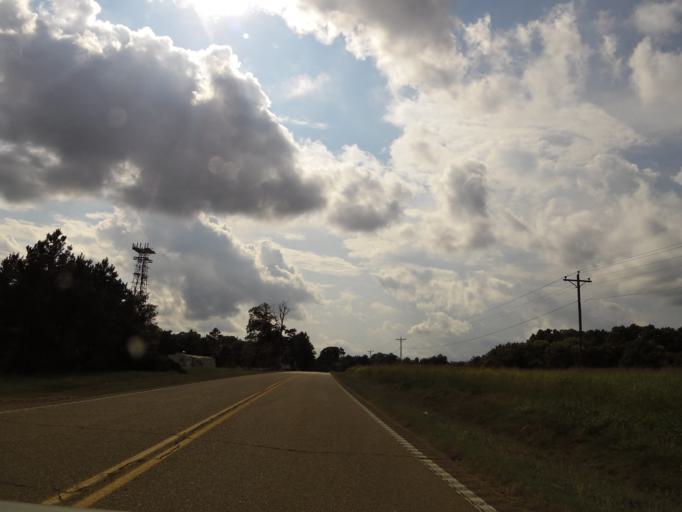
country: US
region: Mississippi
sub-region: Alcorn County
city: Farmington
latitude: 35.0620
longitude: -88.4199
